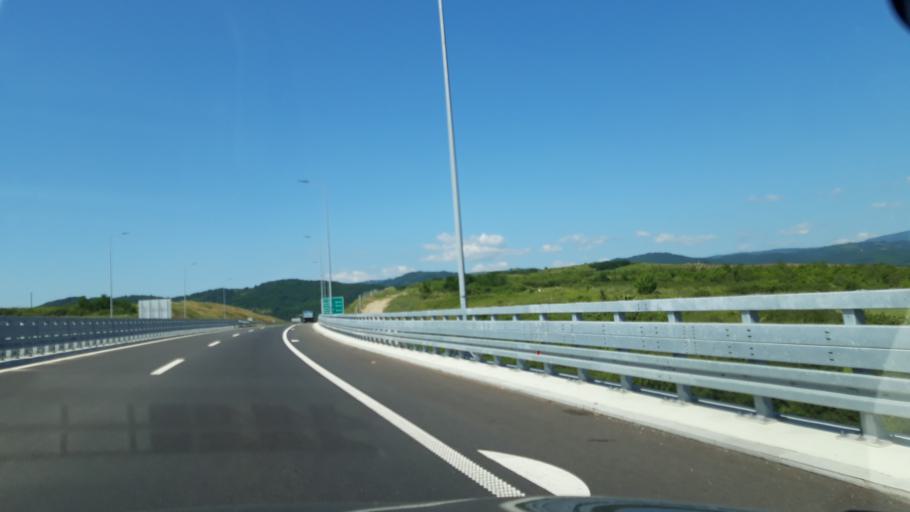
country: RS
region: Central Serbia
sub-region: Pcinjski Okrug
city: Vladicin Han
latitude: 42.7118
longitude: 22.0726
